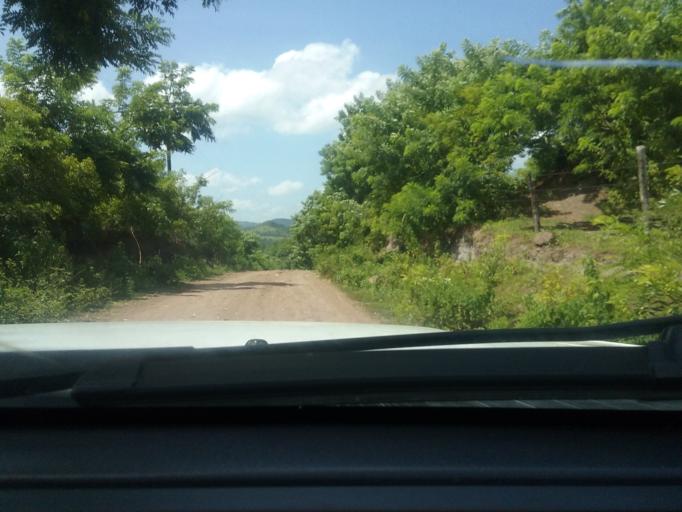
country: NI
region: Matagalpa
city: Terrabona
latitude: 12.6865
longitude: -85.9554
